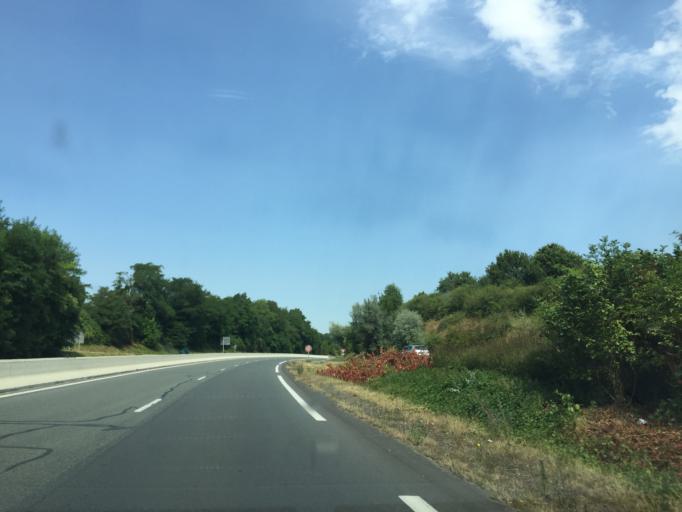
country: FR
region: Poitou-Charentes
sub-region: Departement de la Vienne
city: Biard
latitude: 46.5631
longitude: 0.3029
